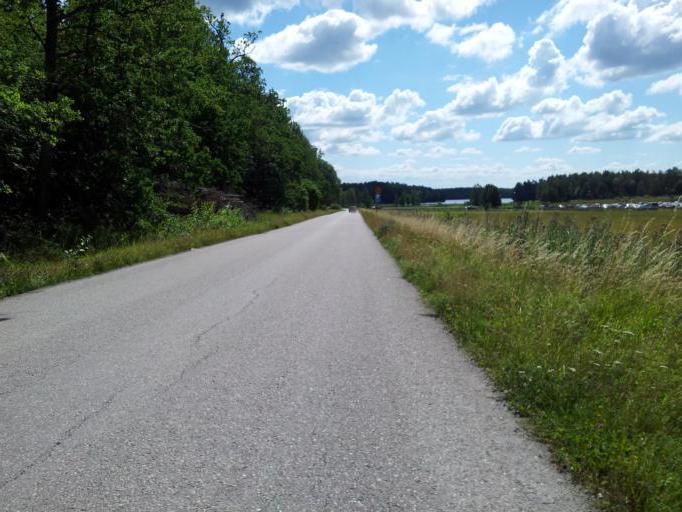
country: SE
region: Uppsala
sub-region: Knivsta Kommun
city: Knivsta
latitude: 59.8386
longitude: 17.9155
